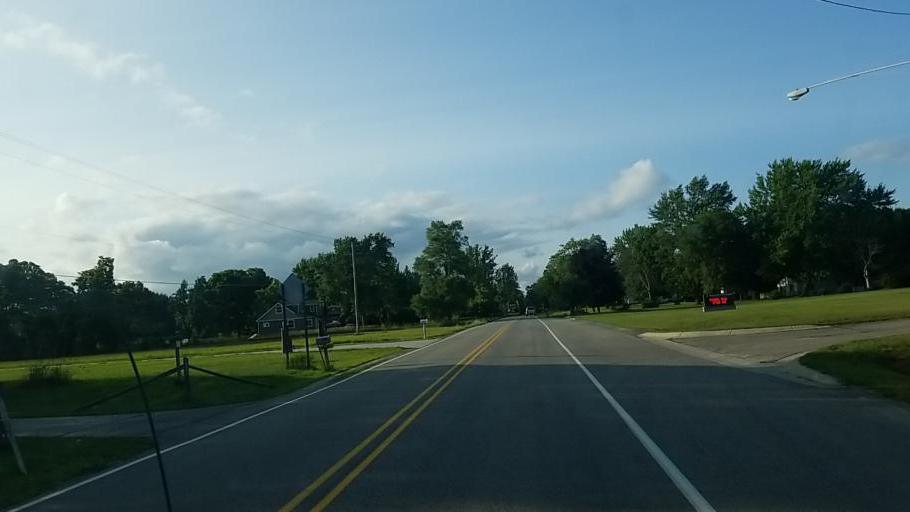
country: US
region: Michigan
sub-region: Montcalm County
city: Greenville
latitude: 43.2380
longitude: -85.3692
